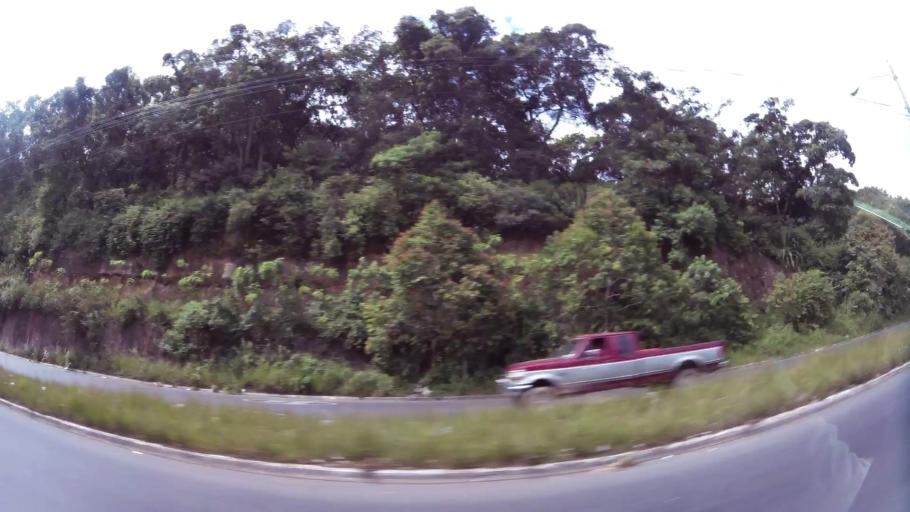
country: GT
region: Guatemala
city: Guatemala City
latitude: 14.6594
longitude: -90.5514
